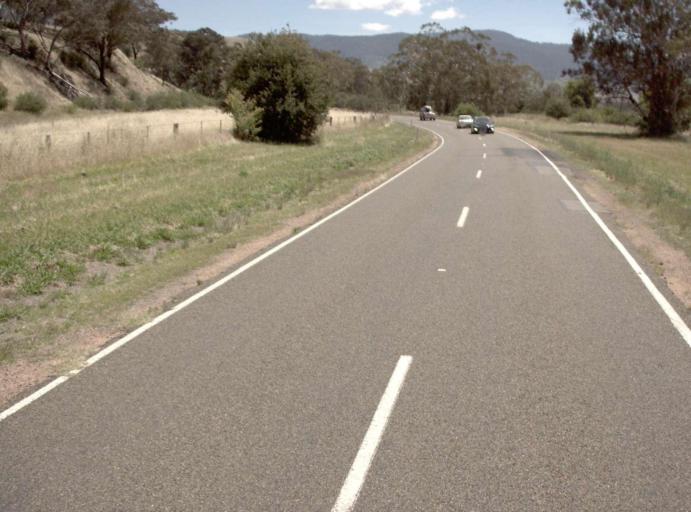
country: AU
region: Victoria
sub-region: East Gippsland
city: Bairnsdale
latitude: -37.2278
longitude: 147.7171
